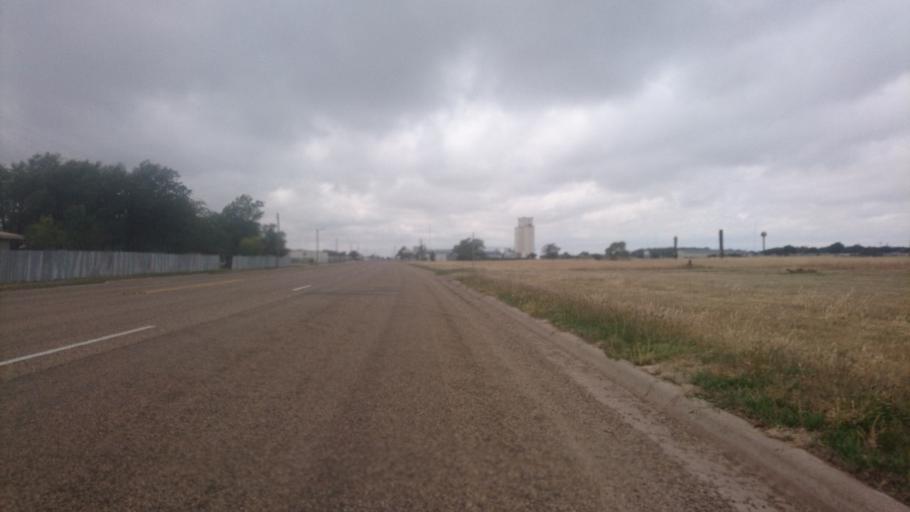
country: US
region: Texas
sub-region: Oldham County
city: Vega
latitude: 35.2431
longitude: -102.4194
